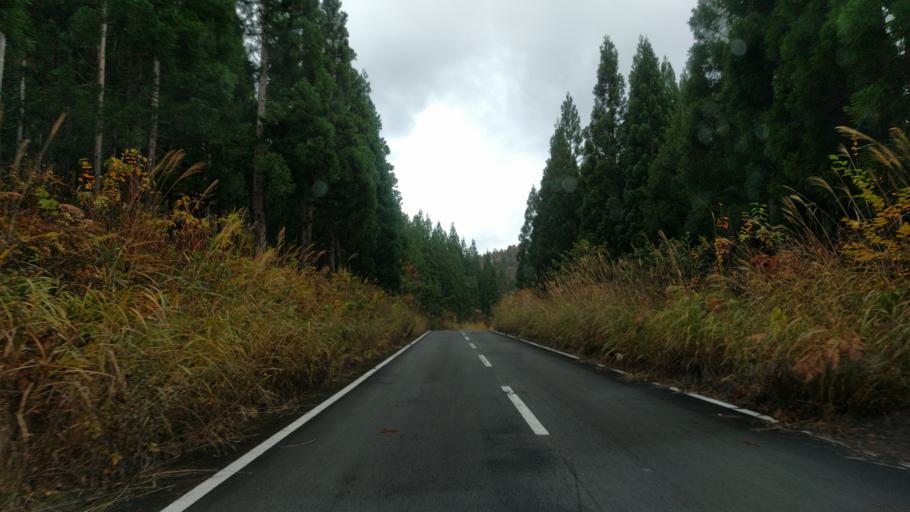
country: JP
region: Fukushima
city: Kitakata
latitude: 37.3792
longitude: 139.7278
